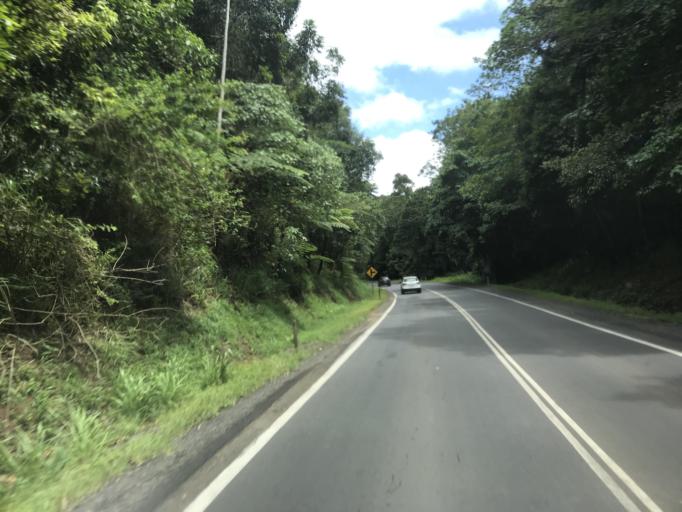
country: AU
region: Queensland
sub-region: Tablelands
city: Ravenshoe
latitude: -17.6015
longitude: 145.7587
